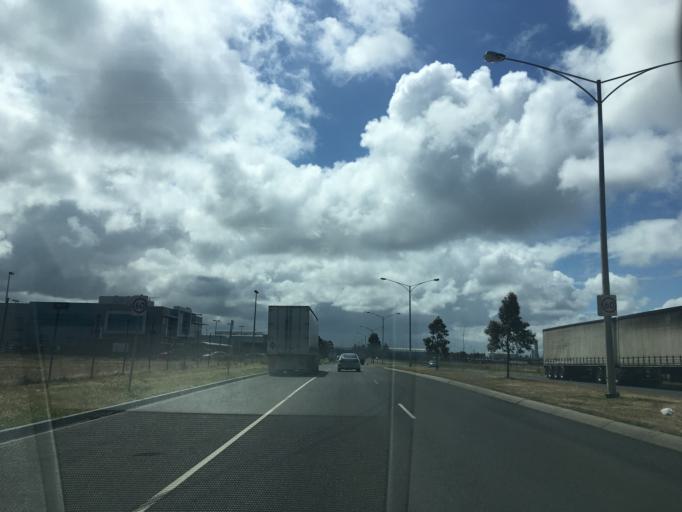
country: AU
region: Victoria
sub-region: Hobsons Bay
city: Altona
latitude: -37.8458
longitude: 144.8095
